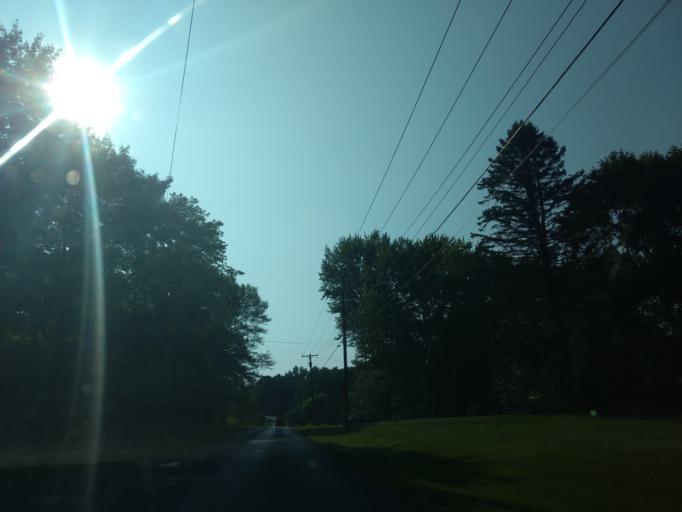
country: US
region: Pennsylvania
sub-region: Lawrence County
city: Ellport
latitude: 40.9667
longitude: -80.2159
